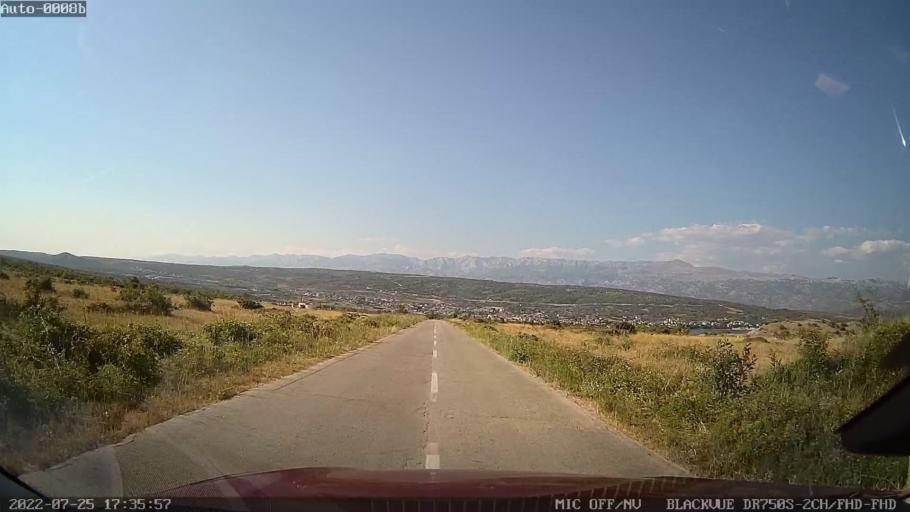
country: HR
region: Zadarska
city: Posedarje
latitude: 44.1956
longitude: 15.4723
